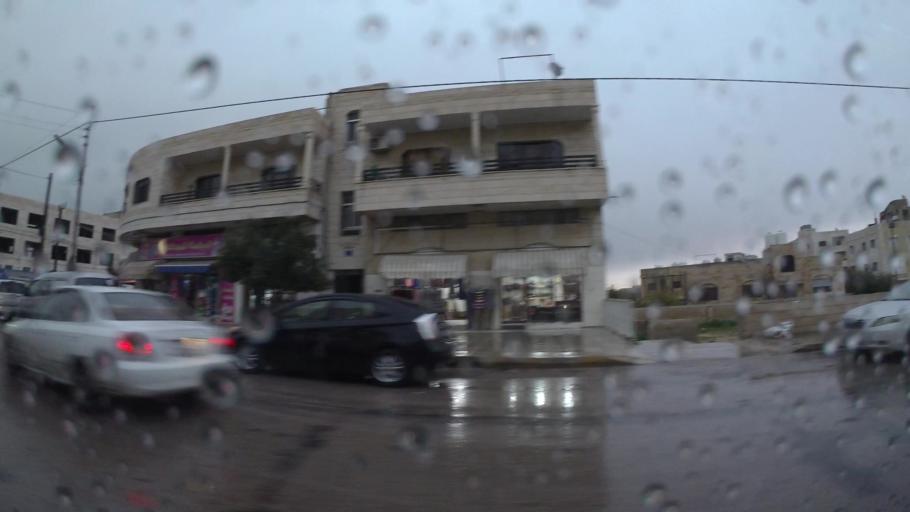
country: JO
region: Amman
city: Amman
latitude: 32.0014
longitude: 35.9691
